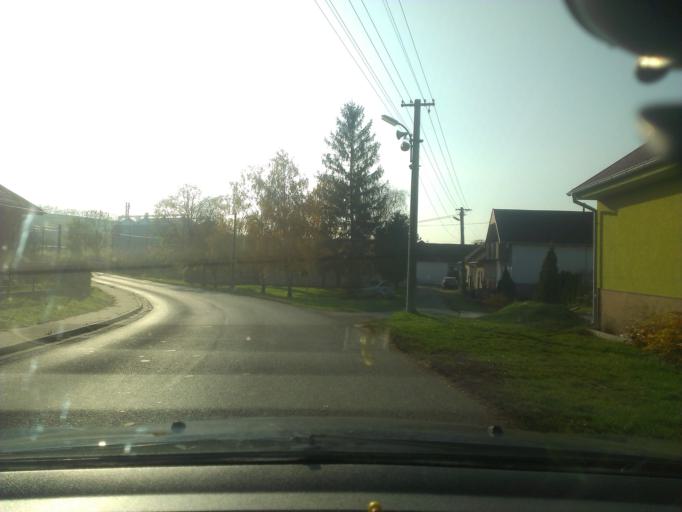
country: SK
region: Trnavsky
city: Hlohovec
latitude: 48.4746
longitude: 17.9884
